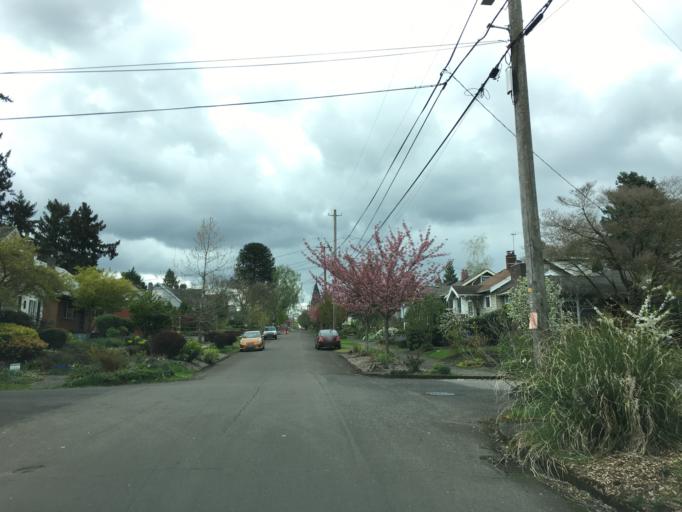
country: US
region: Oregon
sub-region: Multnomah County
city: Lents
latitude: 45.5527
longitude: -122.5878
